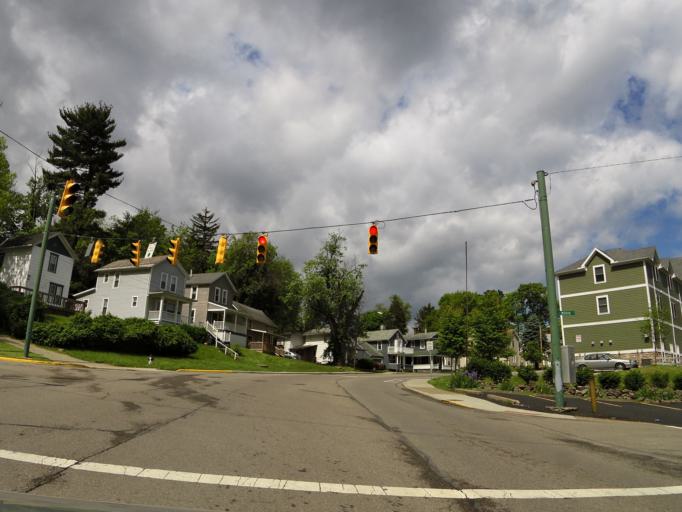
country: US
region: Ohio
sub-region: Athens County
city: Athens
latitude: 39.3325
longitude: -82.1040
